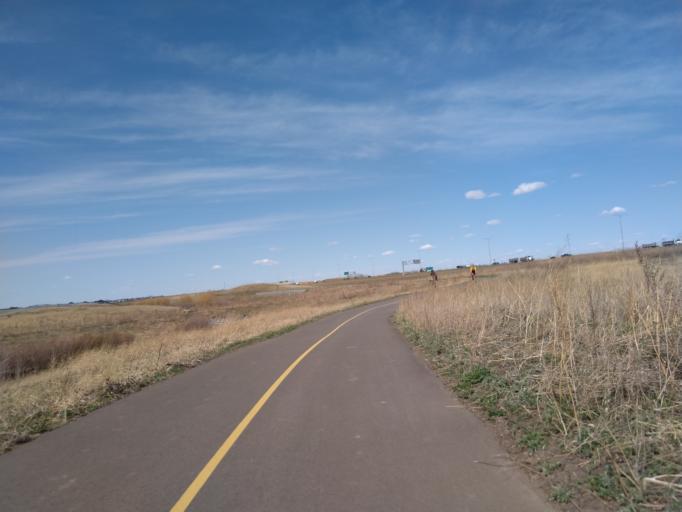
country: CA
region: Alberta
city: Chestermere
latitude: 51.0223
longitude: -113.9243
